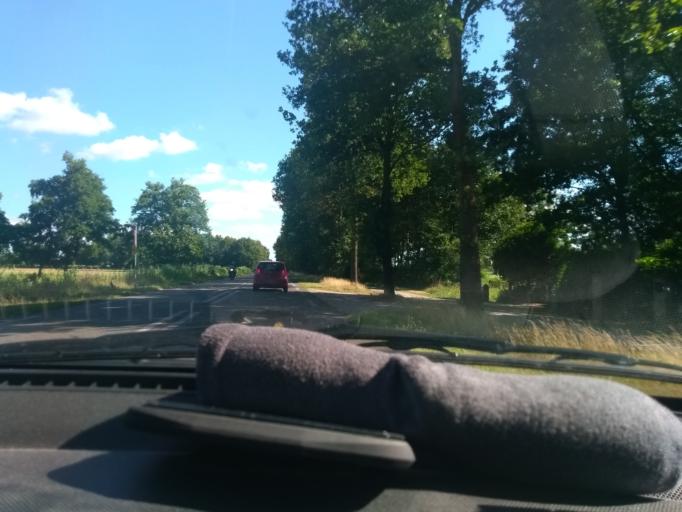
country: NL
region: Drenthe
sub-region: Gemeente Tynaarlo
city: Vries
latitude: 53.1339
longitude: 6.4989
